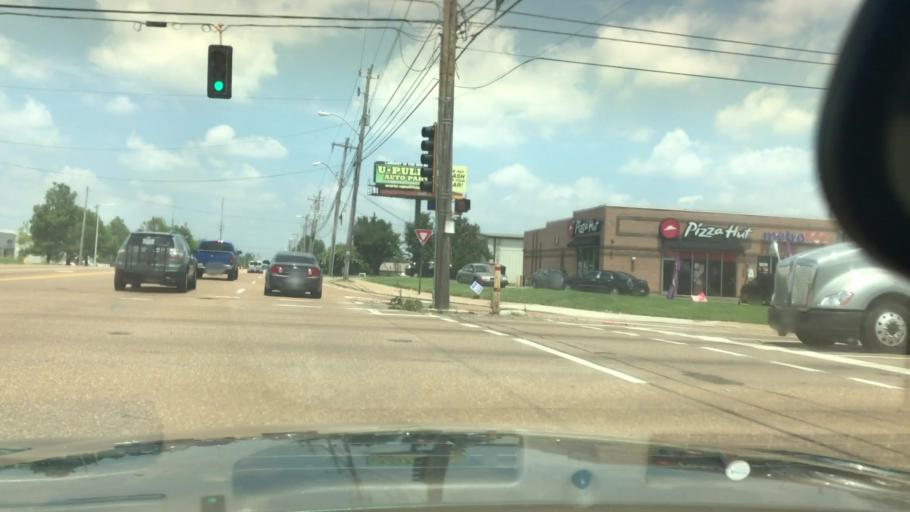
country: US
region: Mississippi
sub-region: De Soto County
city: Southaven
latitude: 35.0206
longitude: -89.9367
